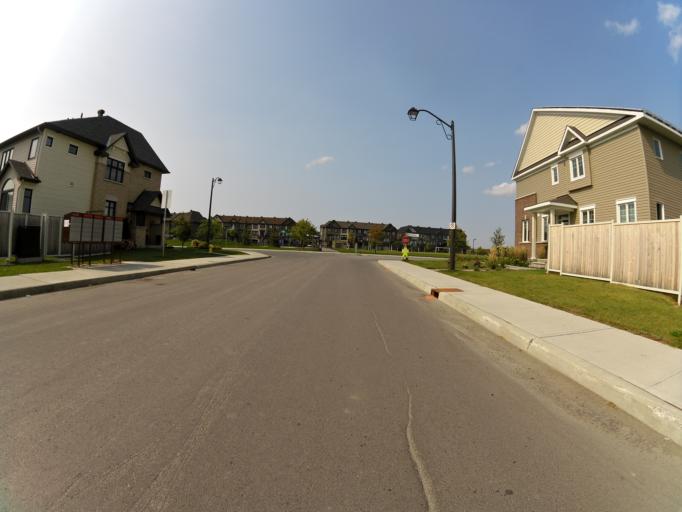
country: CA
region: Ontario
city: Bells Corners
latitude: 45.3043
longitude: -75.9343
